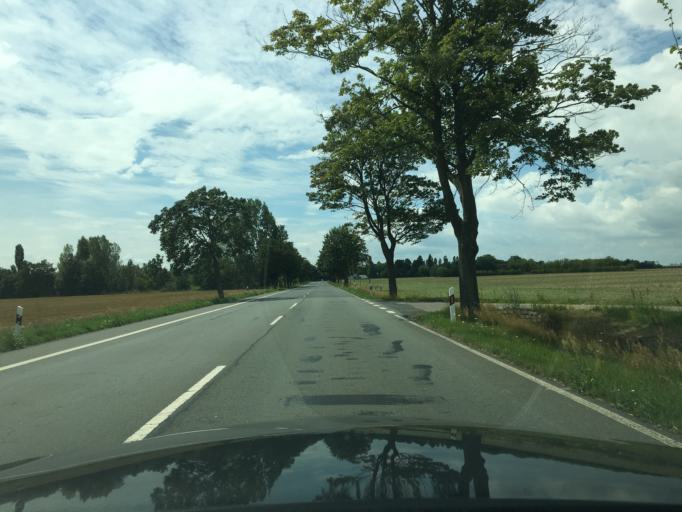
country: DE
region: Saxony-Anhalt
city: Brehna
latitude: 51.5656
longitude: 12.2198
